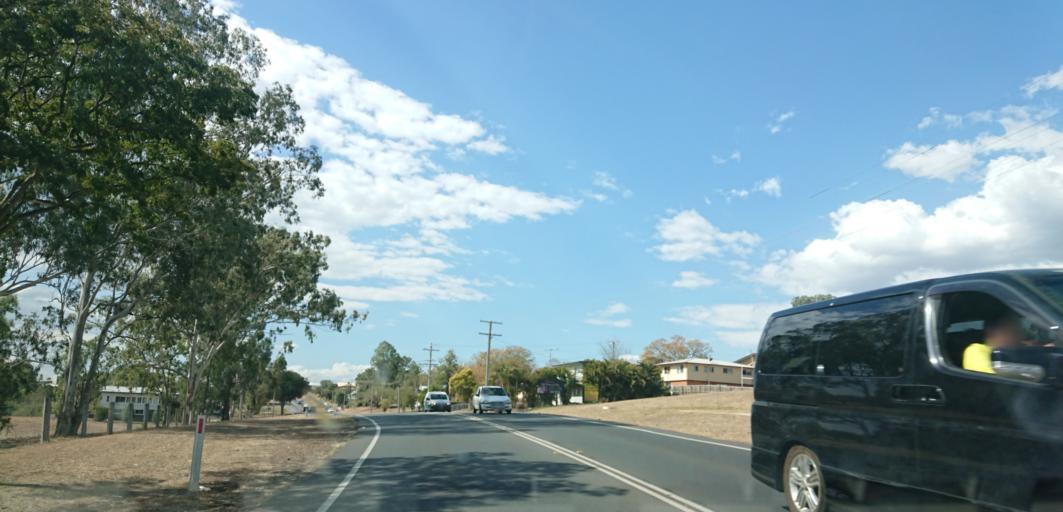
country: AU
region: Queensland
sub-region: Lockyer Valley
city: Gatton
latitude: -27.5682
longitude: 152.2708
